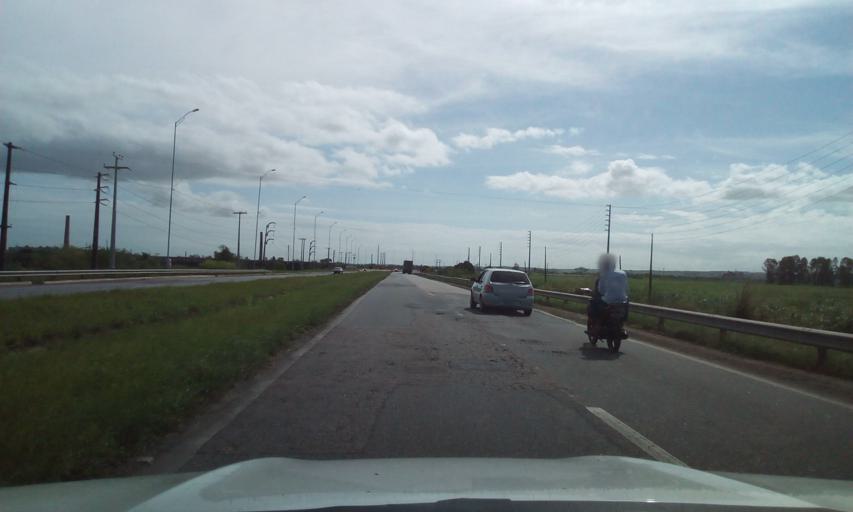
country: BR
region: Paraiba
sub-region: Santa Rita
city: Santa Rita
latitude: -7.1154
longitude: -34.9555
